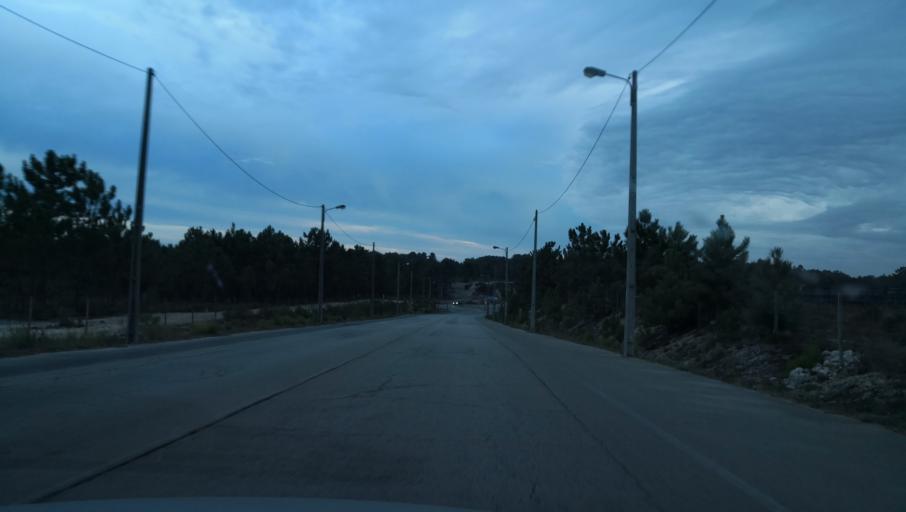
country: PT
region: Setubal
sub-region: Almada
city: Charneca
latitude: 38.5969
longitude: -9.1603
